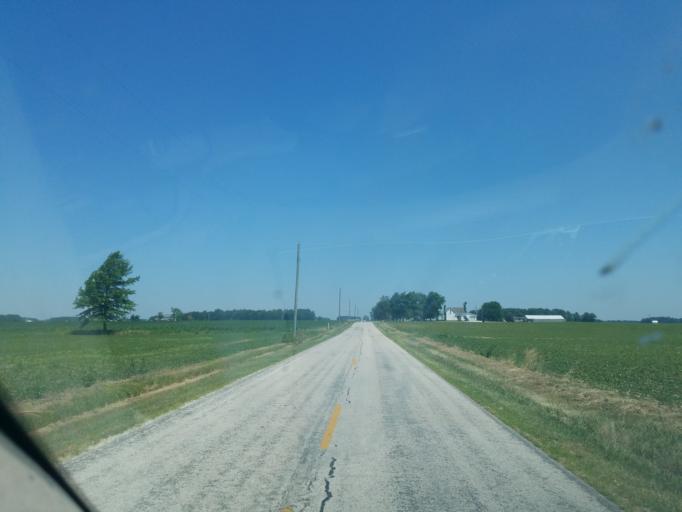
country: US
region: Ohio
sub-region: Mercer County
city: Coldwater
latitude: 40.5775
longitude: -84.7084
